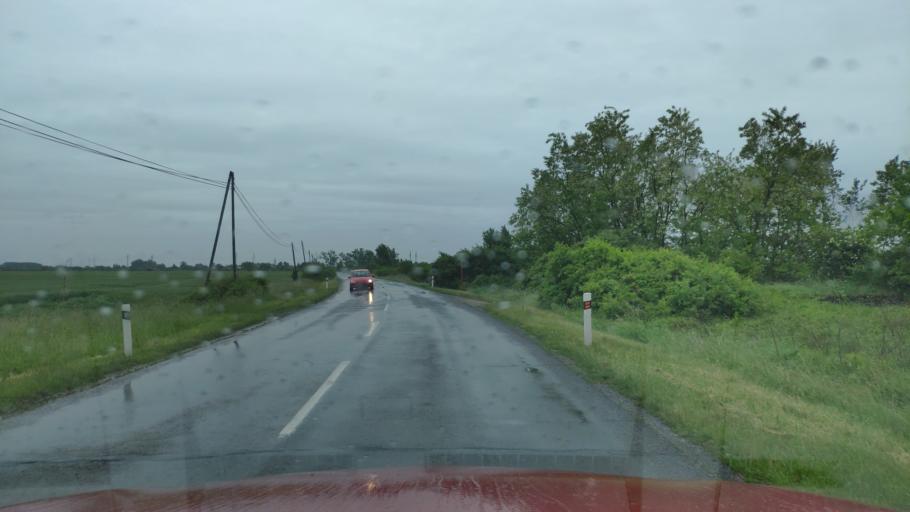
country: SK
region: Kosicky
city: Cierna nad Tisou
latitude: 48.4266
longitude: 22.0219
